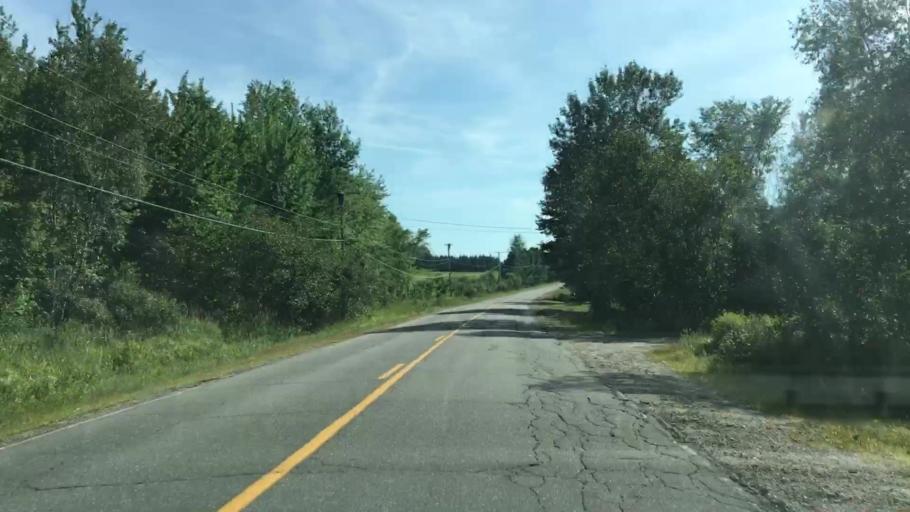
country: US
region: Maine
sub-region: Penobscot County
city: Lincoln
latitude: 45.3223
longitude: -68.5332
